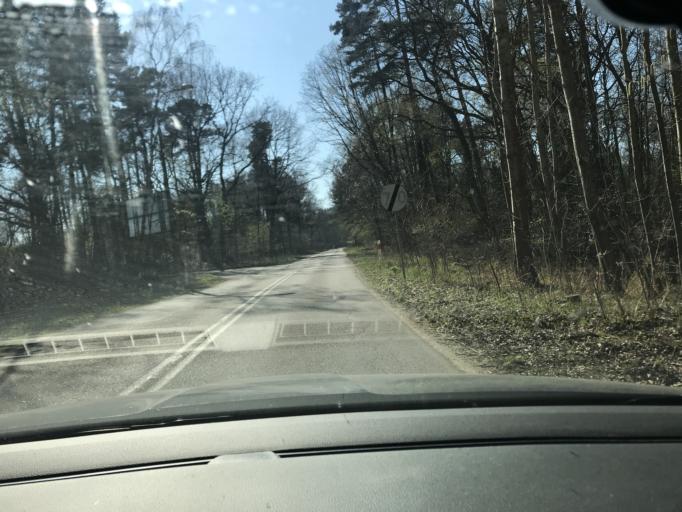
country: PL
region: Pomeranian Voivodeship
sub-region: Powiat nowodworski
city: Krynica Morska
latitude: 54.3693
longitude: 19.4054
